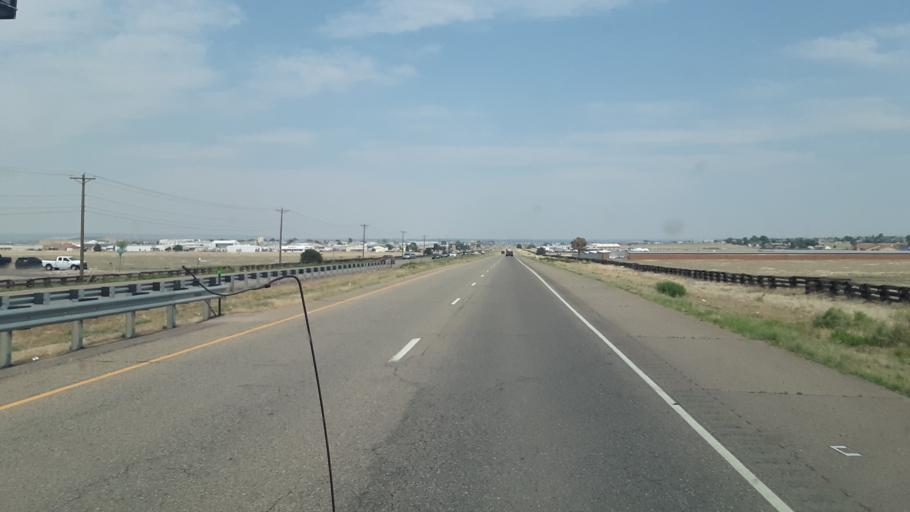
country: US
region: Colorado
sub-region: Pueblo County
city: Pueblo West
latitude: 38.3310
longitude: -104.7273
